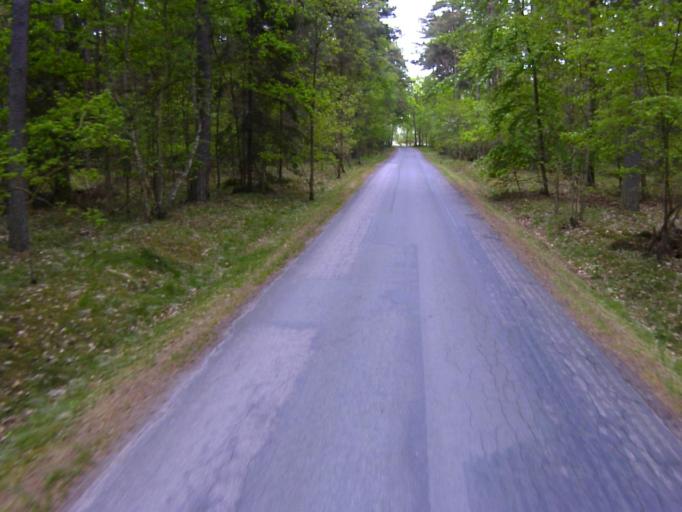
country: SE
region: Skane
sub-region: Kristianstads Kommun
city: Ahus
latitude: 55.9215
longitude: 14.3171
